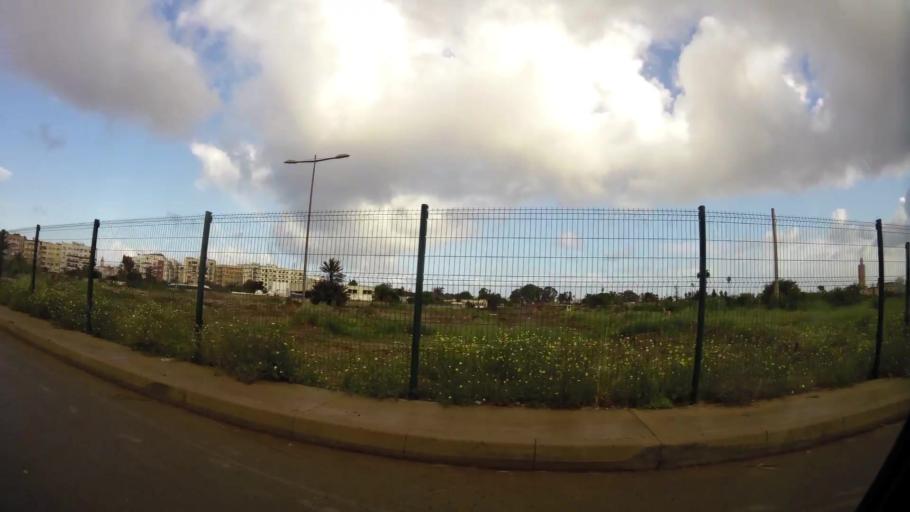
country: MA
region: Grand Casablanca
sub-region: Casablanca
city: Casablanca
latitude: 33.5647
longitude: -7.6648
